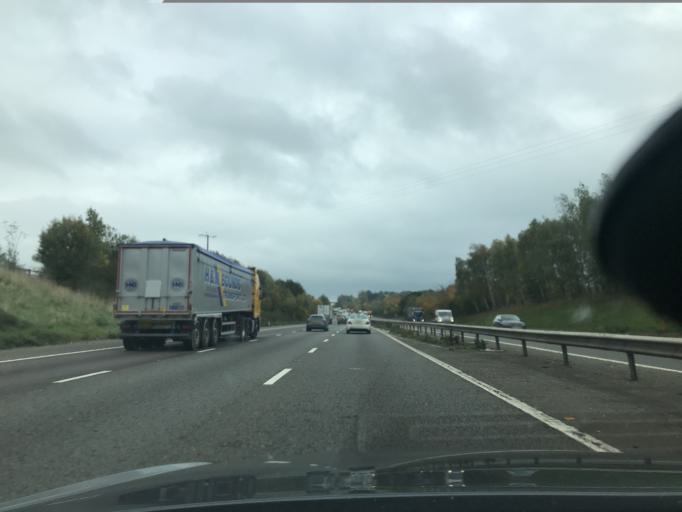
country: GB
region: England
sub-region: Warwickshire
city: Henley in Arden
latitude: 52.3316
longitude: -1.7543
